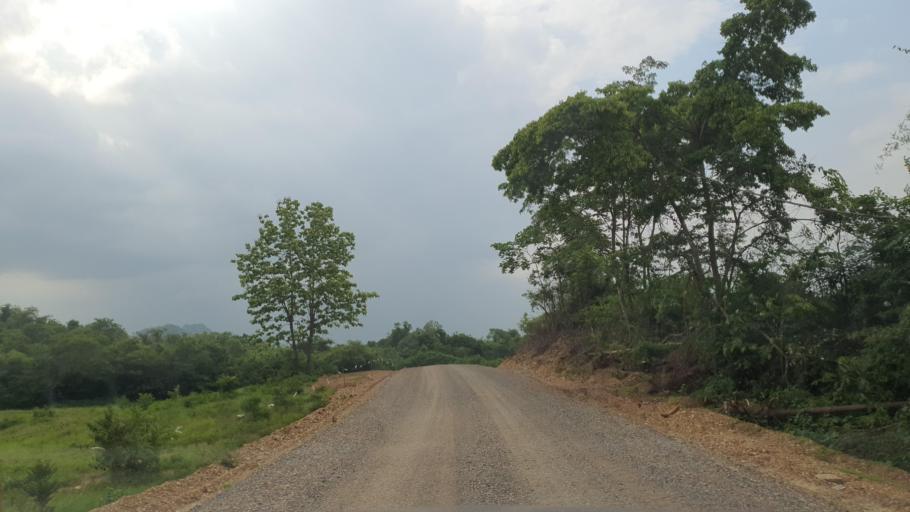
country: TH
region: Sukhothai
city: Thung Saliam
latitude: 17.2614
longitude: 99.5384
